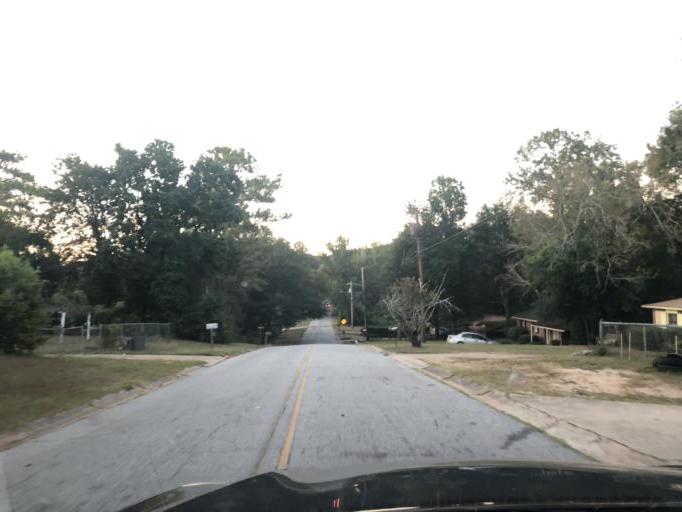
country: US
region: Georgia
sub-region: Muscogee County
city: Columbus
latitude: 32.4703
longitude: -84.8994
